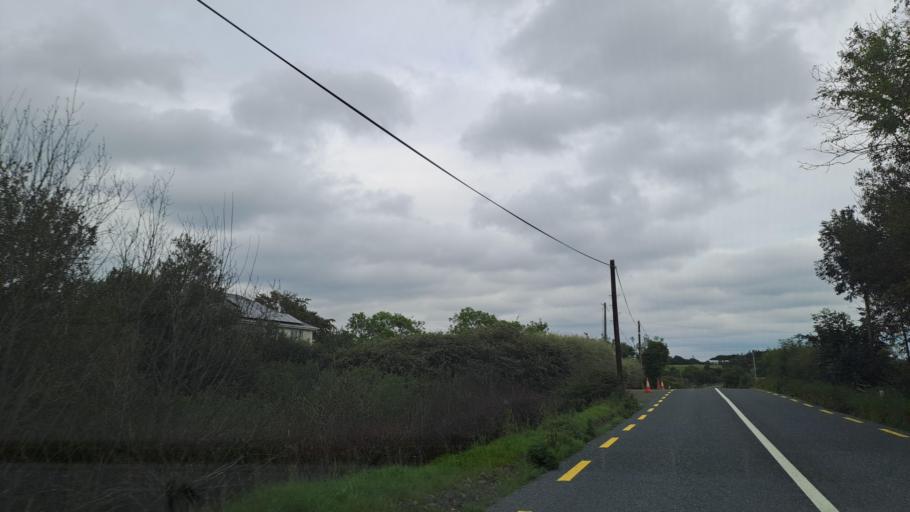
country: IE
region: Ulster
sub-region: An Cabhan
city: Bailieborough
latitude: 53.9546
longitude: -6.9484
